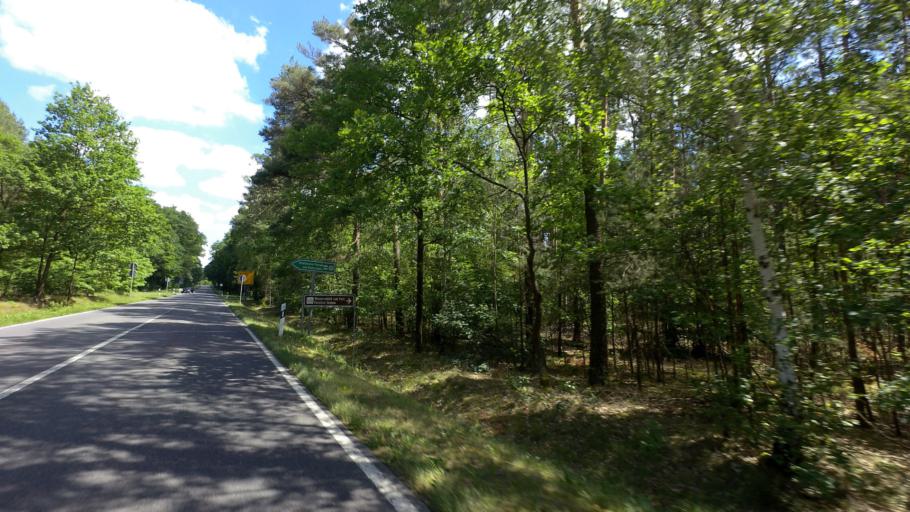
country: DE
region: Brandenburg
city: Sonnewalde
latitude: 51.7557
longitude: 13.6807
